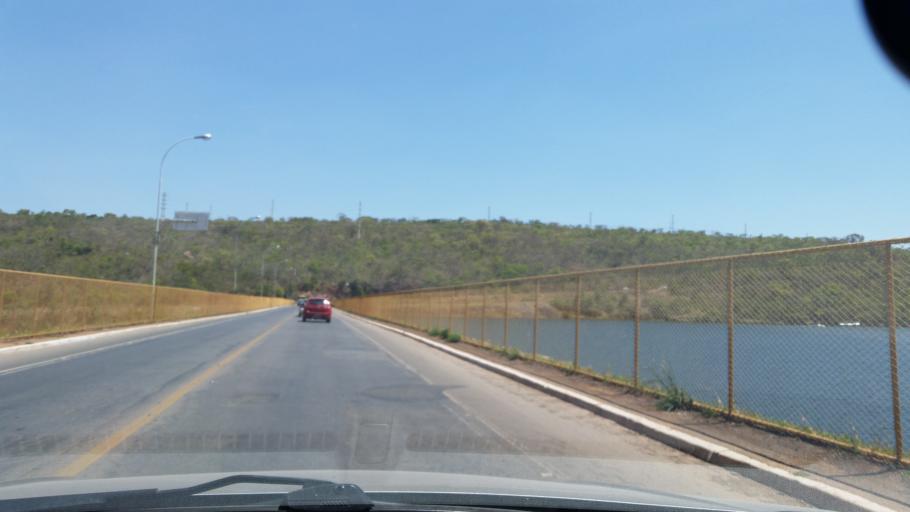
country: BR
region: Federal District
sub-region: Brasilia
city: Brasilia
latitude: -15.7995
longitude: -47.7847
